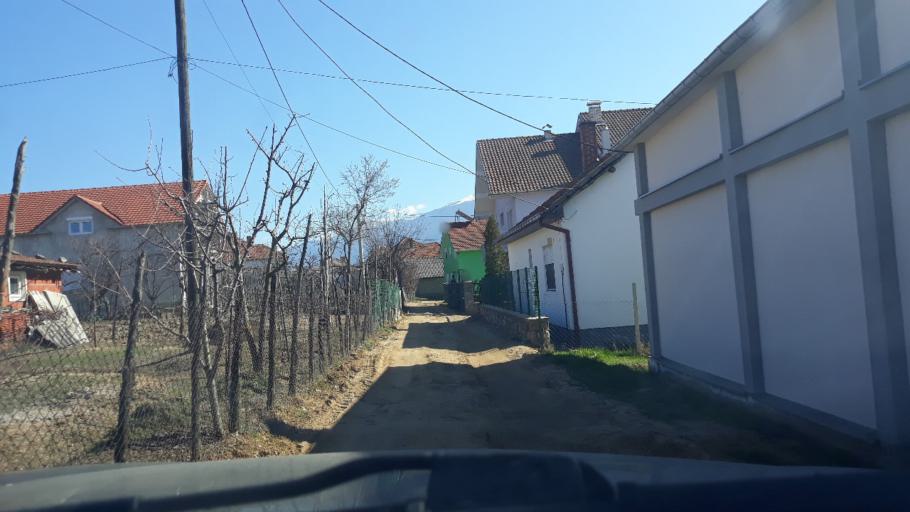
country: MK
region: Novo Selo
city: Novo Selo
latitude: 41.4178
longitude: 22.8791
